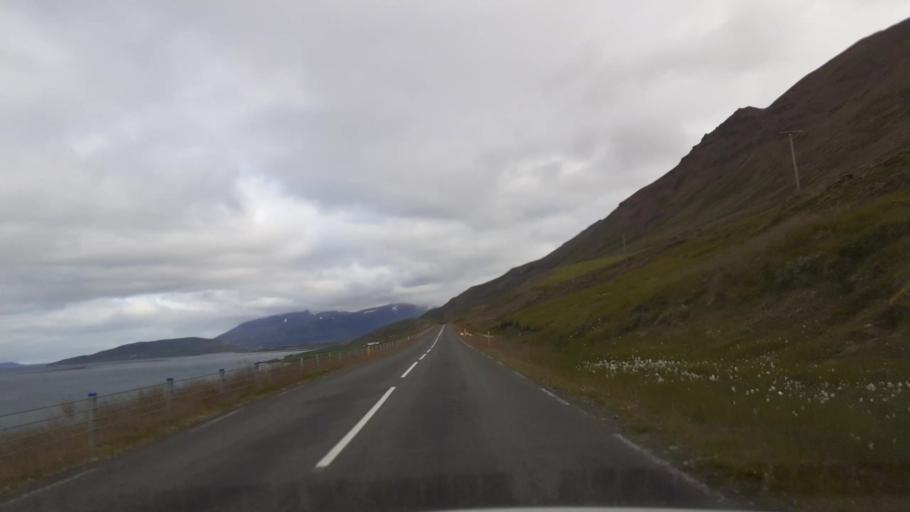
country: IS
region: Northeast
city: Akureyri
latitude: 65.8383
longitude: -18.0557
